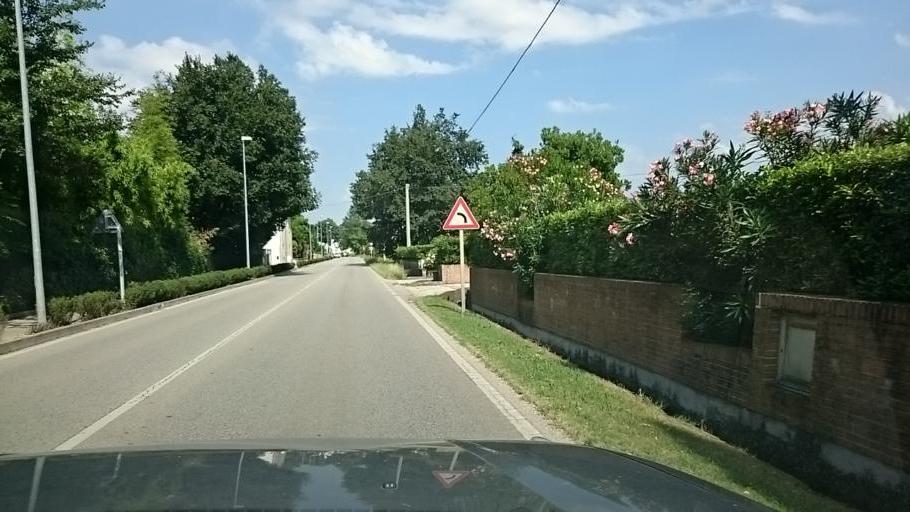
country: IT
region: Veneto
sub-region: Provincia di Vicenza
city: Rosa
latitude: 45.7218
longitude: 11.7380
